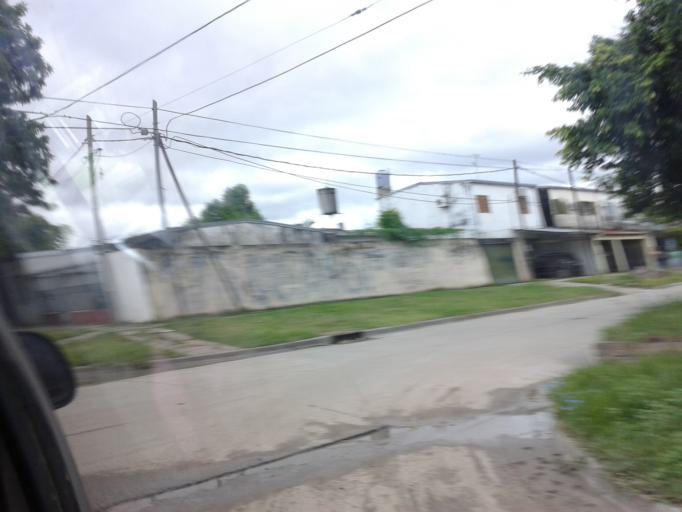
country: AR
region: Formosa
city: Formosa
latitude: -26.1665
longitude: -58.1977
